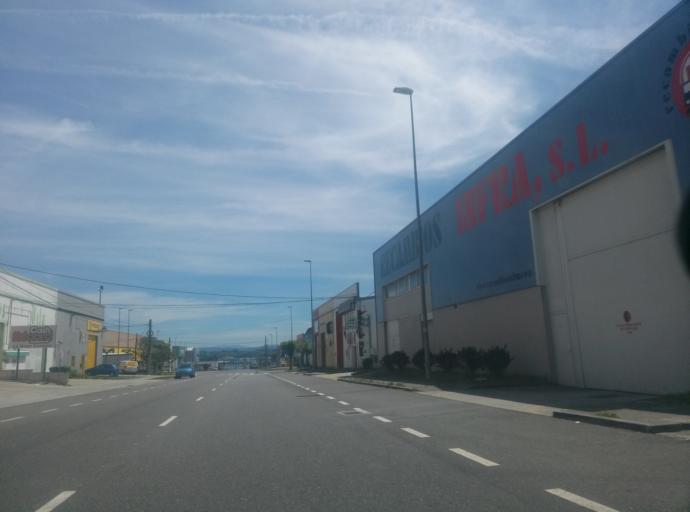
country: ES
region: Galicia
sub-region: Provincia de Lugo
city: Lugo
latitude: 43.0472
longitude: -7.5653
